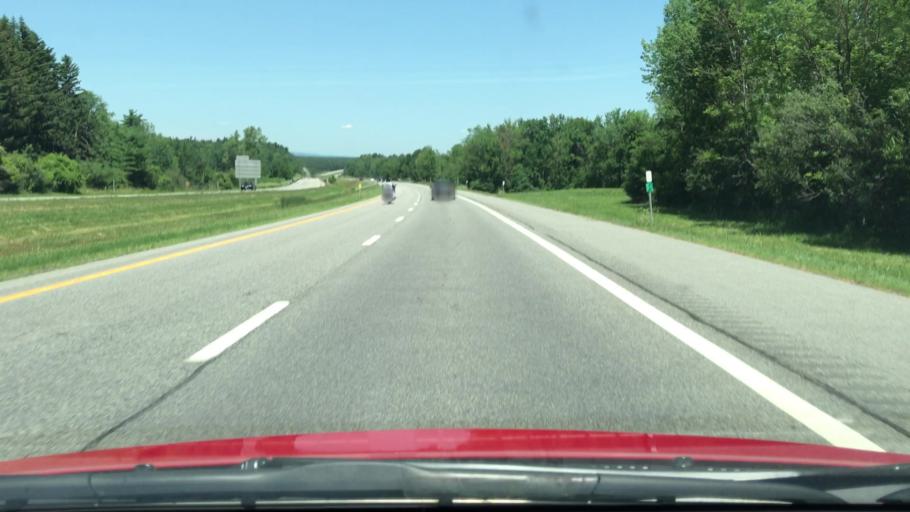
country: US
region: New York
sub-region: Essex County
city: Keeseville
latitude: 44.4636
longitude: -73.4852
